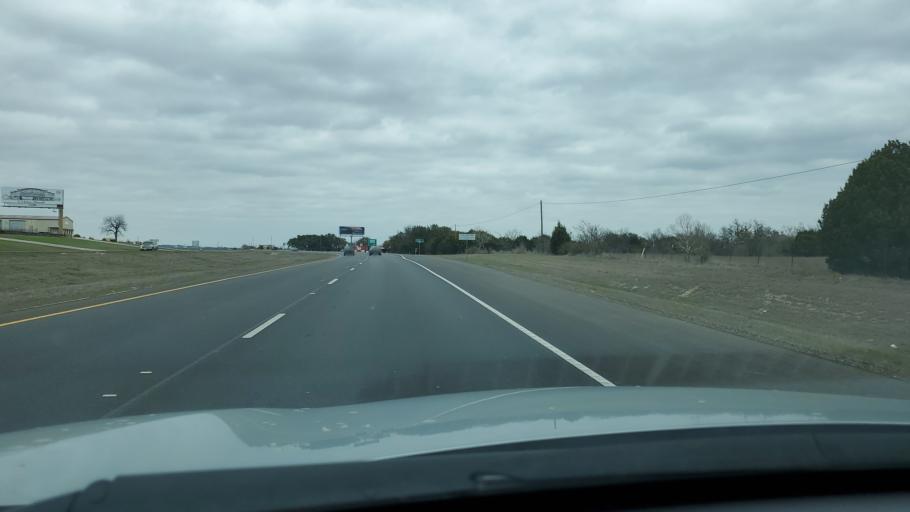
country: US
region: Texas
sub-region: Bell County
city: Killeen
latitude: 31.0037
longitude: -97.7545
